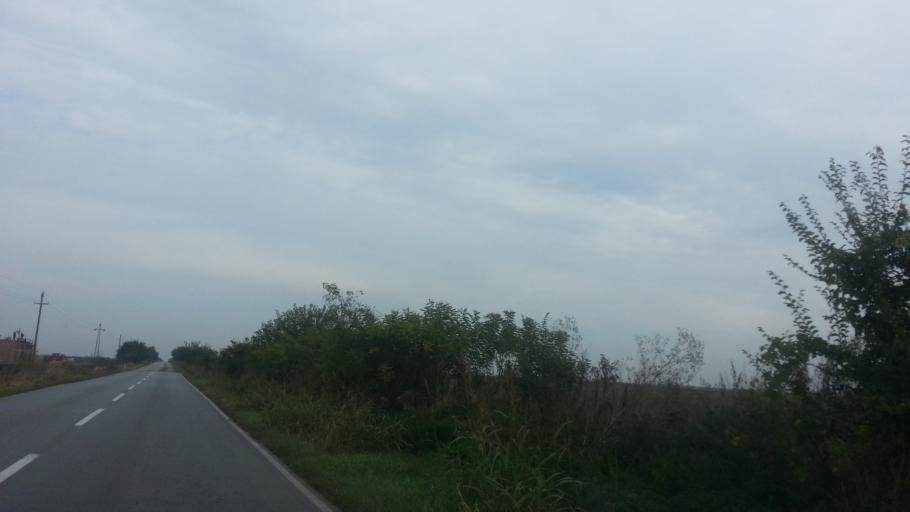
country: RS
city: Belegis
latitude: 45.0439
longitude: 20.3328
